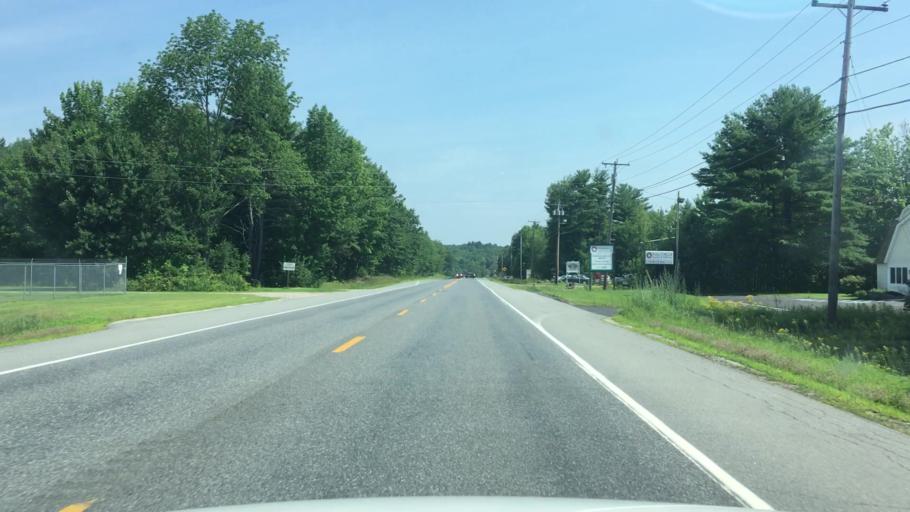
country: US
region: Maine
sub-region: Kennebec County
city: Winthrop
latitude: 44.2854
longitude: -69.9988
